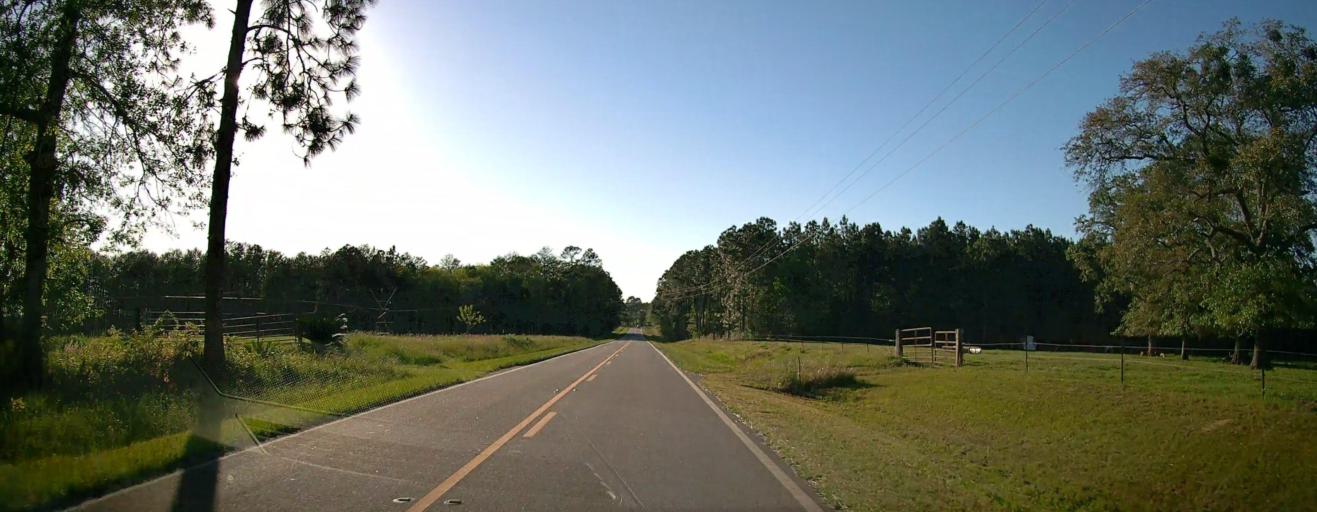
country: US
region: Georgia
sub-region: Ben Hill County
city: Fitzgerald
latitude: 31.6845
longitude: -83.2078
